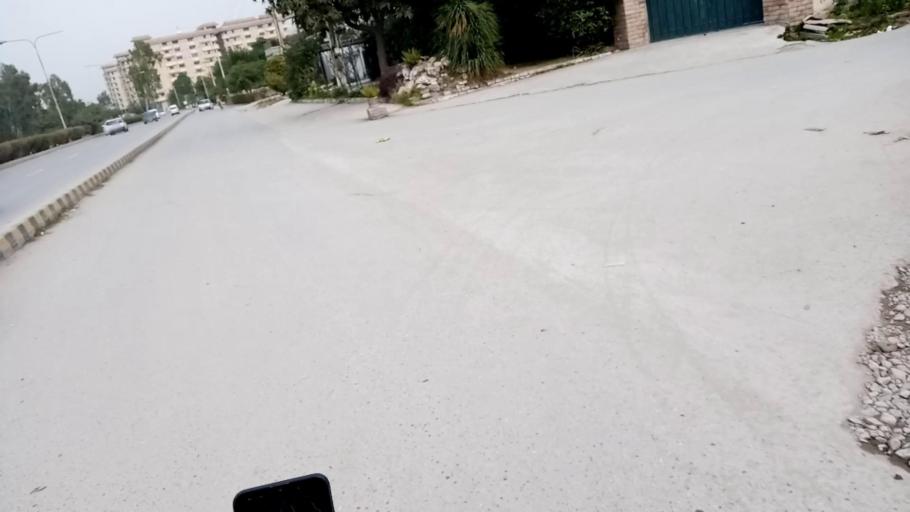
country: PK
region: Khyber Pakhtunkhwa
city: Peshawar
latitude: 33.9670
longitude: 71.4345
